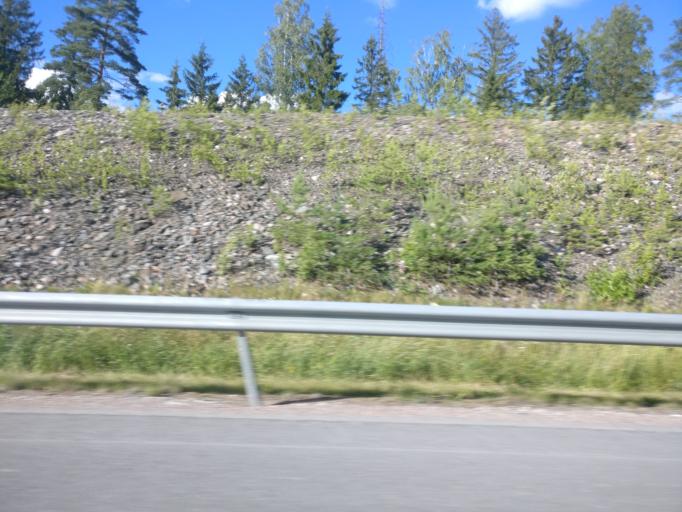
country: FI
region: Uusimaa
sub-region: Helsinki
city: Saukkola
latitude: 60.3235
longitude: 23.9576
